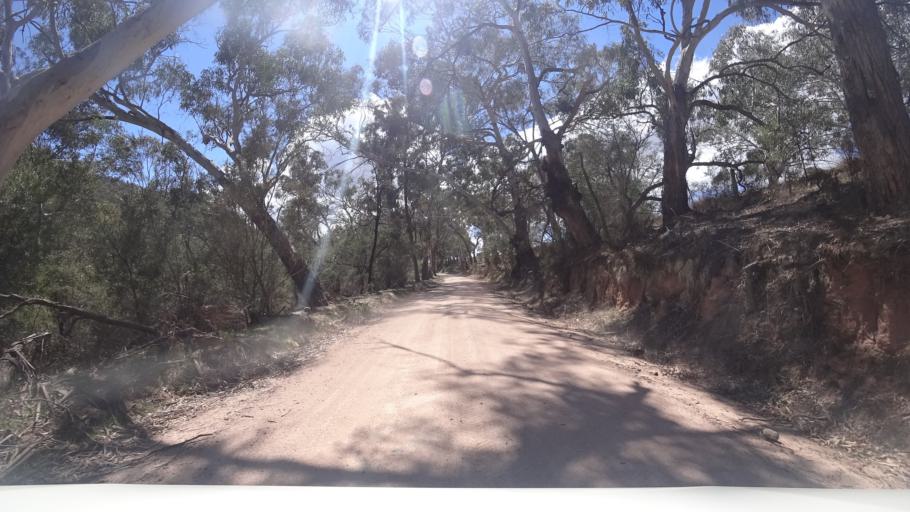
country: AU
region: New South Wales
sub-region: Oberon
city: Oberon
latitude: -33.5428
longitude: 149.9324
